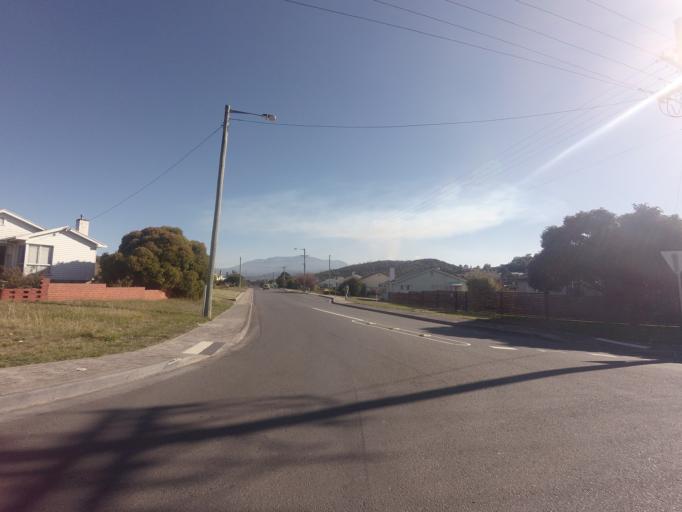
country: AU
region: Tasmania
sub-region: Clarence
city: Warrane
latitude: -42.8571
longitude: 147.3812
